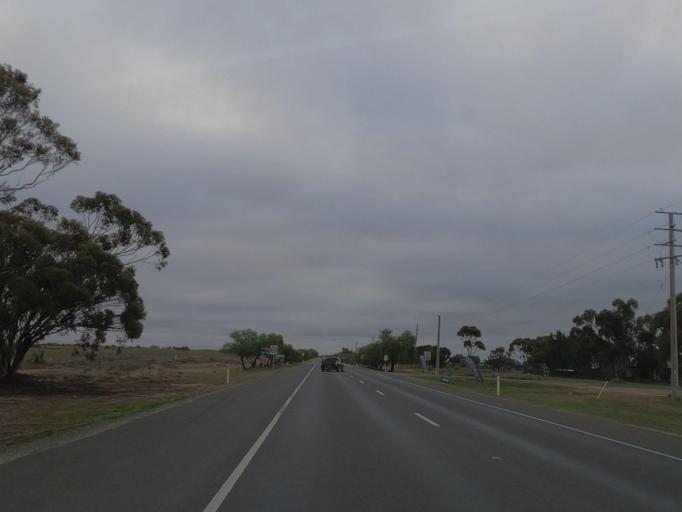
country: AU
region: Victoria
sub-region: Swan Hill
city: Swan Hill
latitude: -35.4504
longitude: 143.6241
